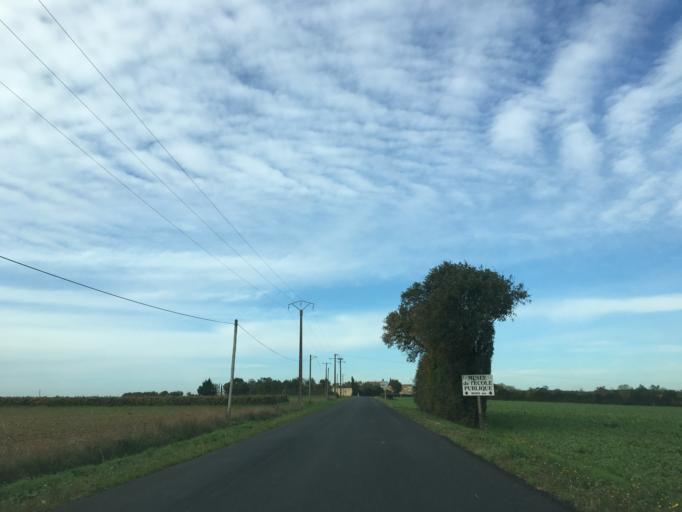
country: FR
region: Poitou-Charentes
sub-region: Departement des Deux-Sevres
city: Beauvoir-sur-Niort
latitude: 46.0718
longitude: -0.5022
